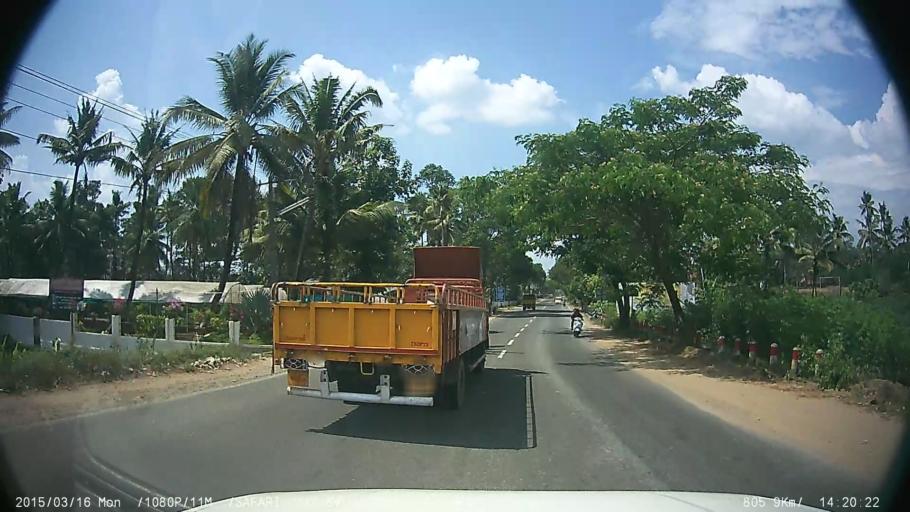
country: IN
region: Kerala
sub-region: Ernakulam
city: Muvattupula
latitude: 10.0494
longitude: 76.5316
